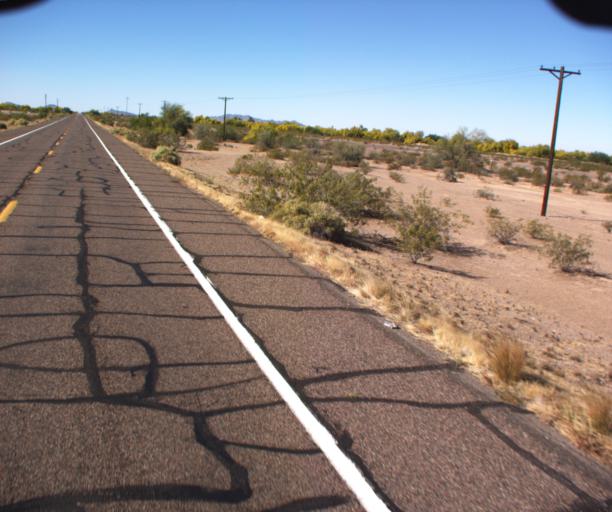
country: US
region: Arizona
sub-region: Maricopa County
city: Gila Bend
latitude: 32.9053
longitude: -112.7405
